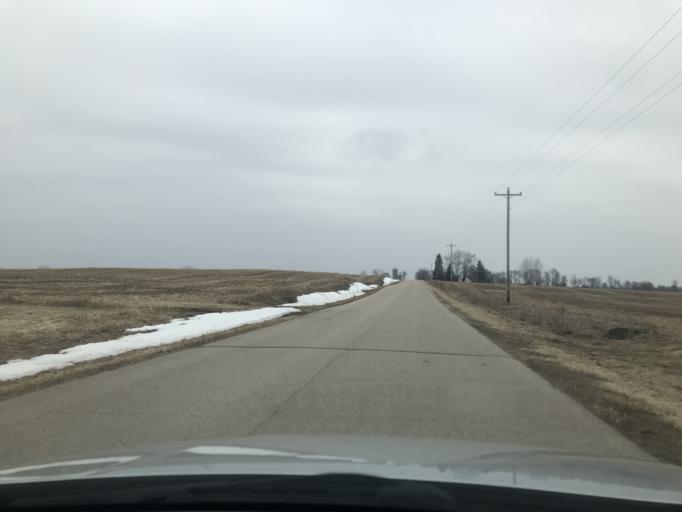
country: US
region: Wisconsin
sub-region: Marinette County
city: Peshtigo
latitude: 45.0503
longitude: -87.8509
